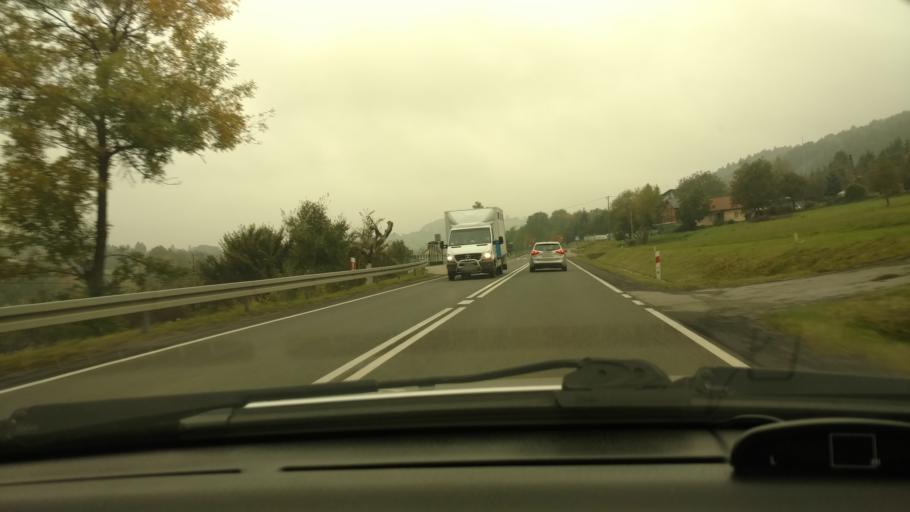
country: PL
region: Lesser Poland Voivodeship
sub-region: Powiat nowosadecki
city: Grybow
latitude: 49.6235
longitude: 20.9266
